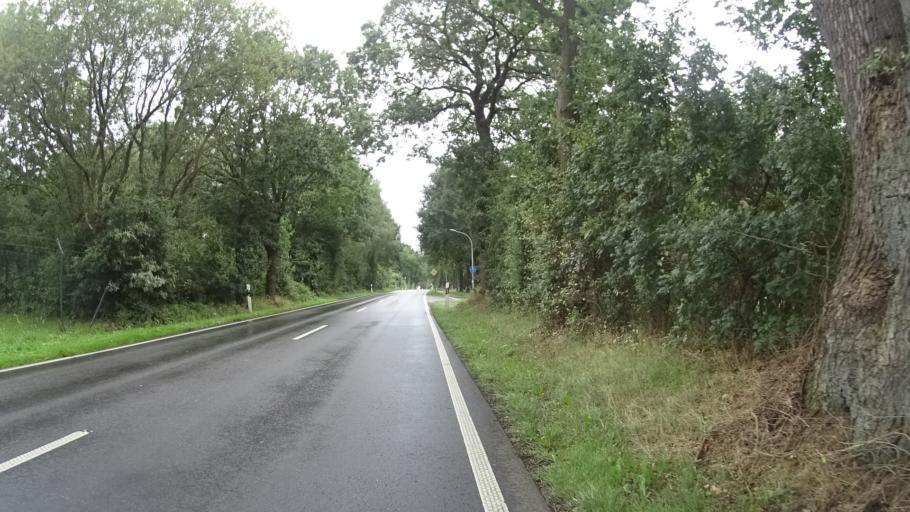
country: DE
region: Schleswig-Holstein
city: Alveslohe
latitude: 53.7894
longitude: 9.9272
